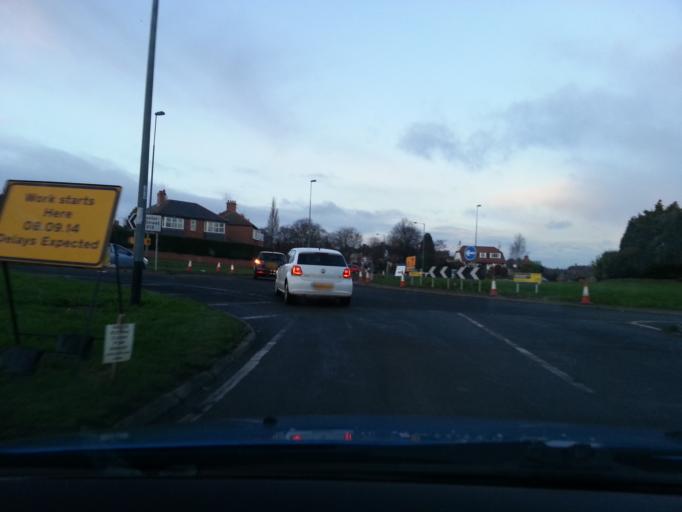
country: GB
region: England
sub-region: County Durham
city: Chester-le-Street
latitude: 54.8616
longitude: -1.5686
